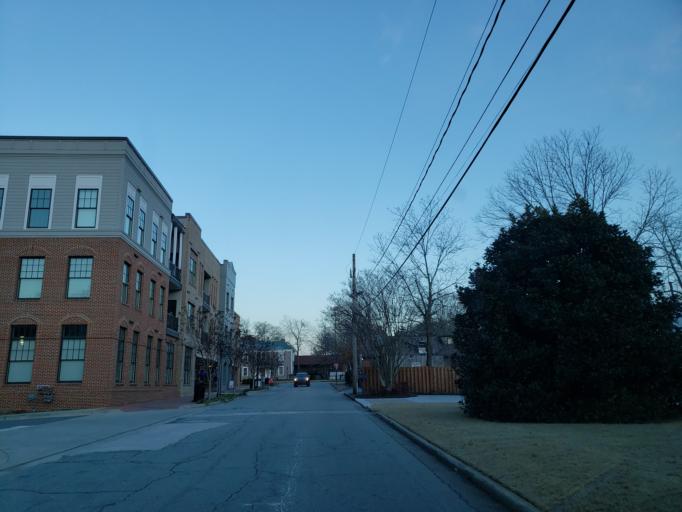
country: US
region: Georgia
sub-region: Fulton County
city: Roswell
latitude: 34.0307
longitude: -84.3625
